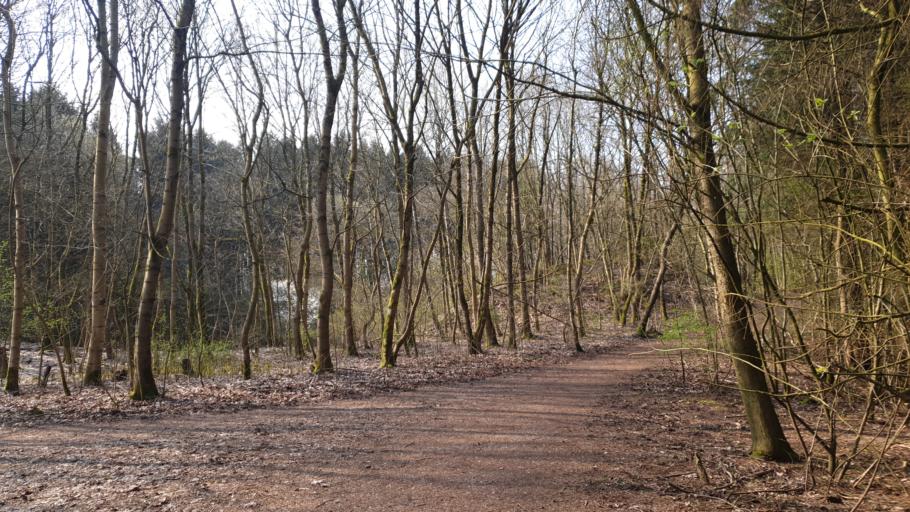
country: DK
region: Central Jutland
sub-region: Hedensted Kommune
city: Hedensted
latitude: 55.8103
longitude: 9.6974
